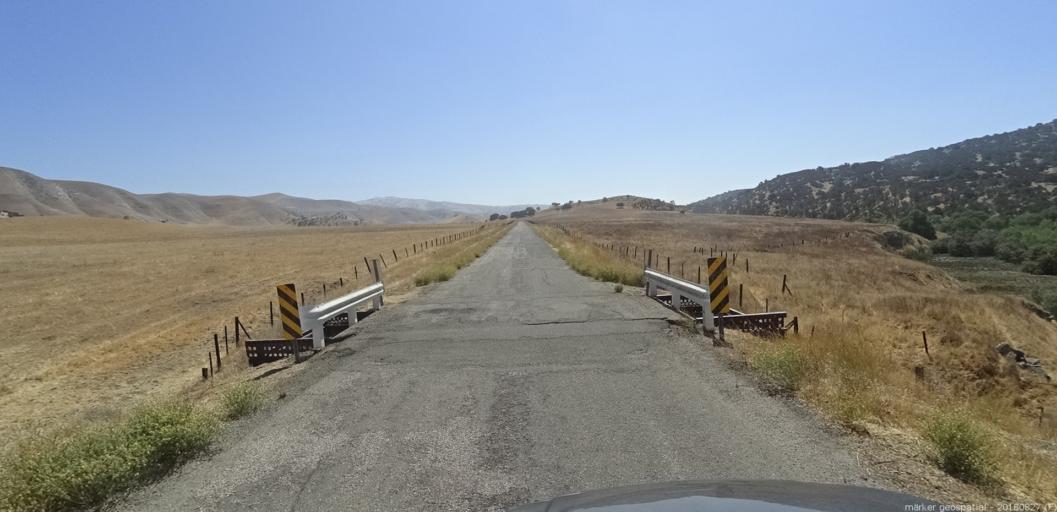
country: US
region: California
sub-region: Monterey County
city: King City
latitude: 36.2950
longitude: -120.9857
